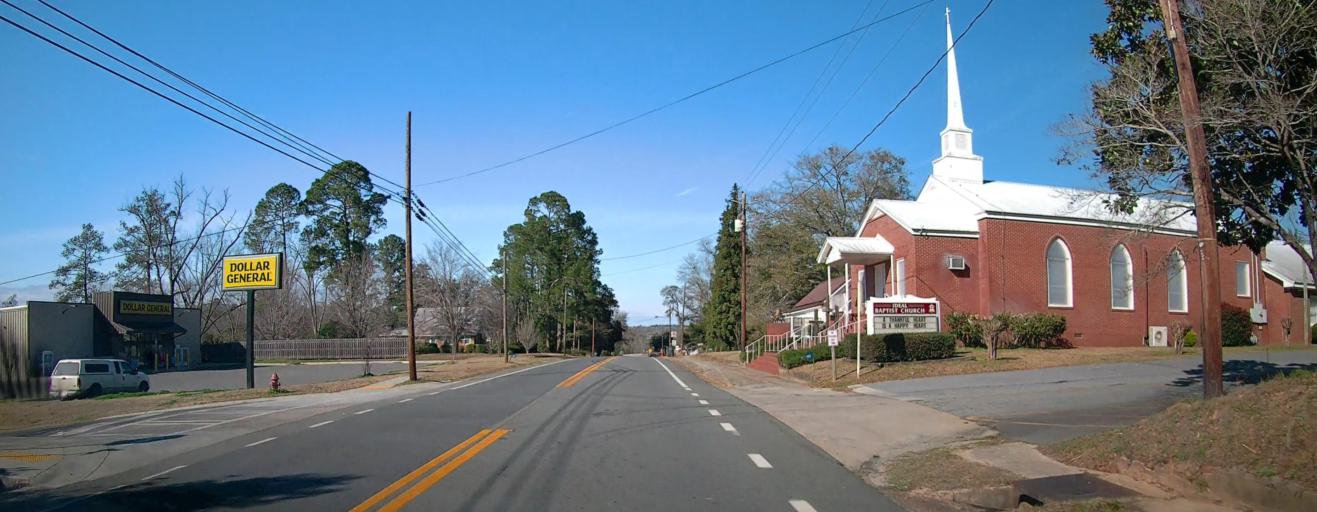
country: US
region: Georgia
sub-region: Macon County
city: Oglethorpe
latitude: 32.3733
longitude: -84.1883
